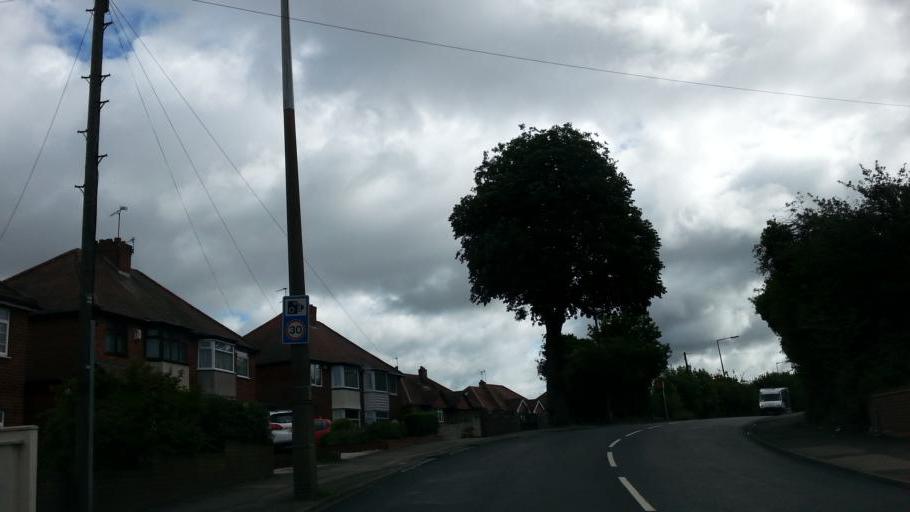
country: GB
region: England
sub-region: Dudley
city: Halesowen
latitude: 52.4550
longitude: -2.0684
